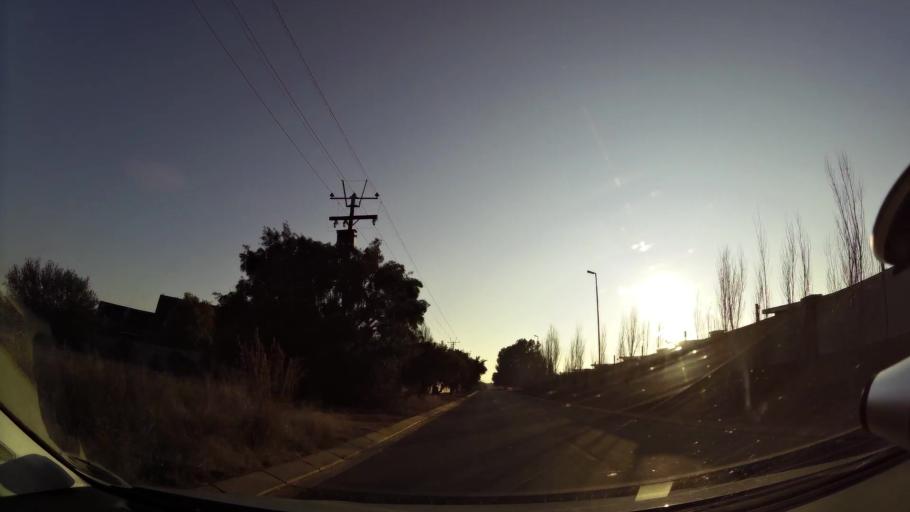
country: ZA
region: Orange Free State
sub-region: Mangaung Metropolitan Municipality
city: Bloemfontein
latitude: -29.0822
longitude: 26.1470
